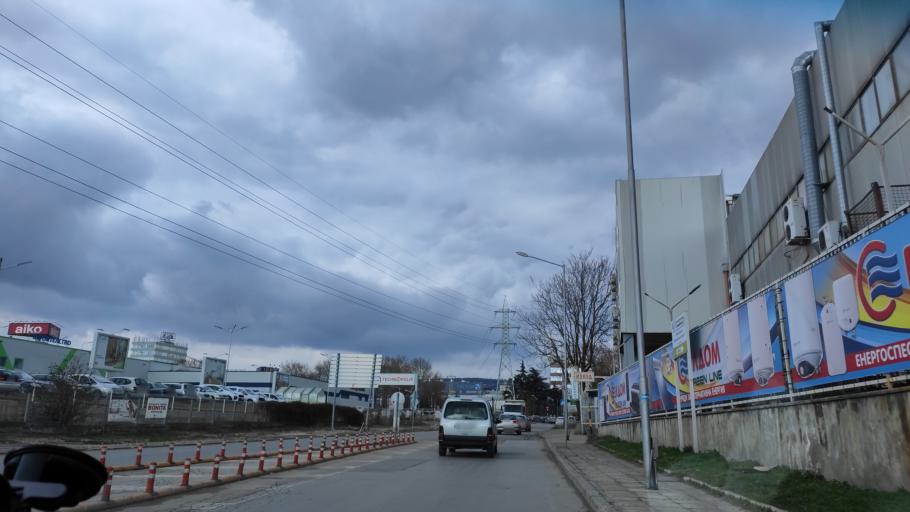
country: BG
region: Varna
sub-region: Obshtina Varna
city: Varna
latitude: 43.2198
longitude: 27.8744
